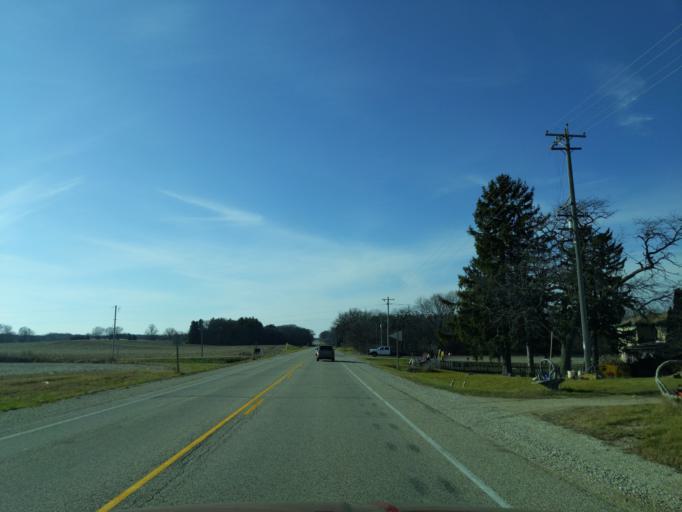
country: US
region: Wisconsin
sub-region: Rock County
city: Milton
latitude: 42.8265
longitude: -88.8847
